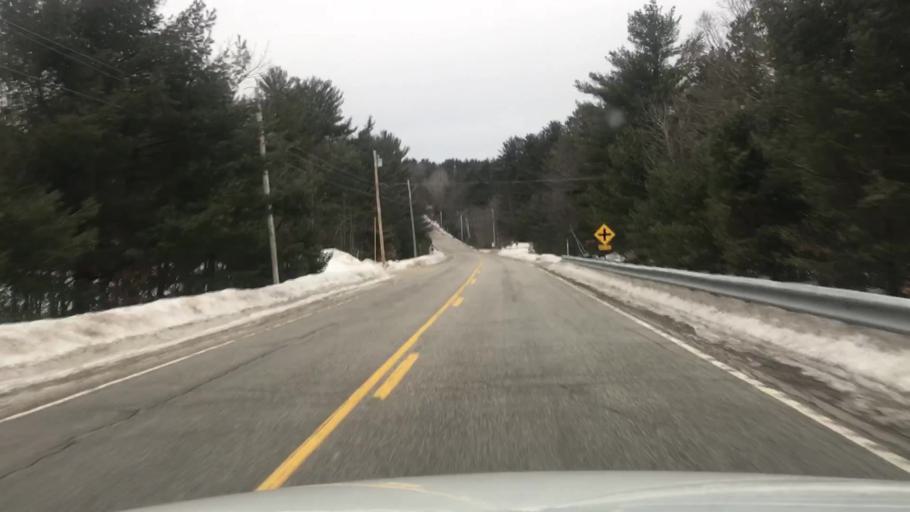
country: US
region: Maine
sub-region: York County
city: Newfield
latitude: 43.6008
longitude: -70.8833
